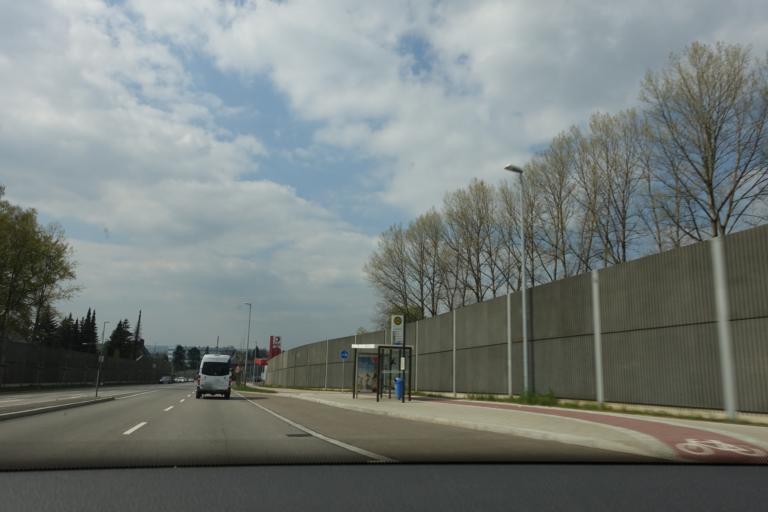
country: DE
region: Saxony
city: Chemnitz
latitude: 50.8092
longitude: 12.9662
